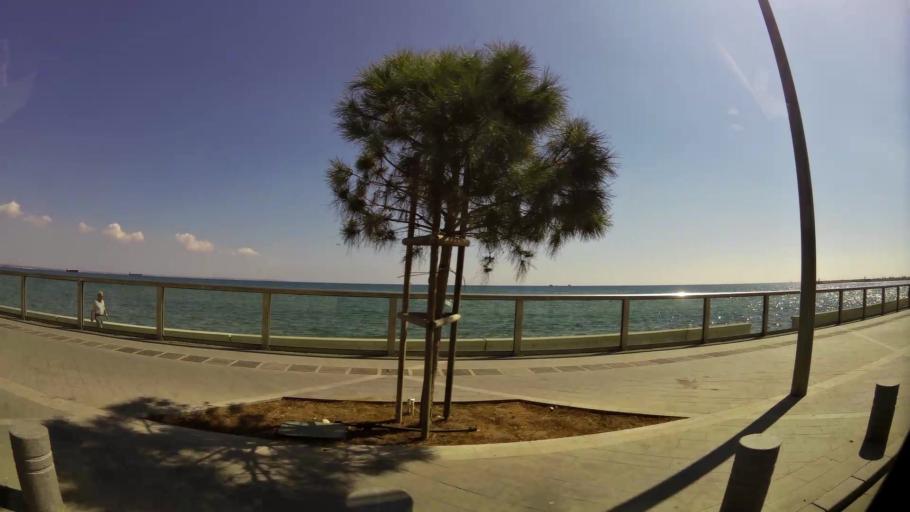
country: CY
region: Larnaka
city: Larnaca
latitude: 34.9036
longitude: 33.6377
